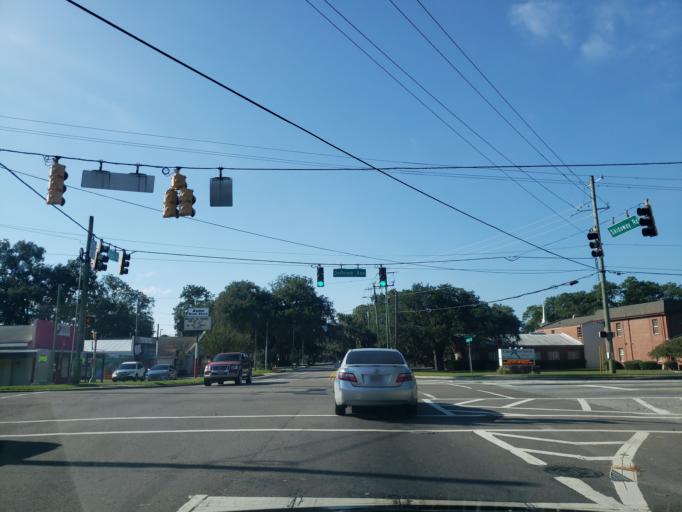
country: US
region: Georgia
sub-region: Chatham County
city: Thunderbolt
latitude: 32.0195
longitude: -81.0750
